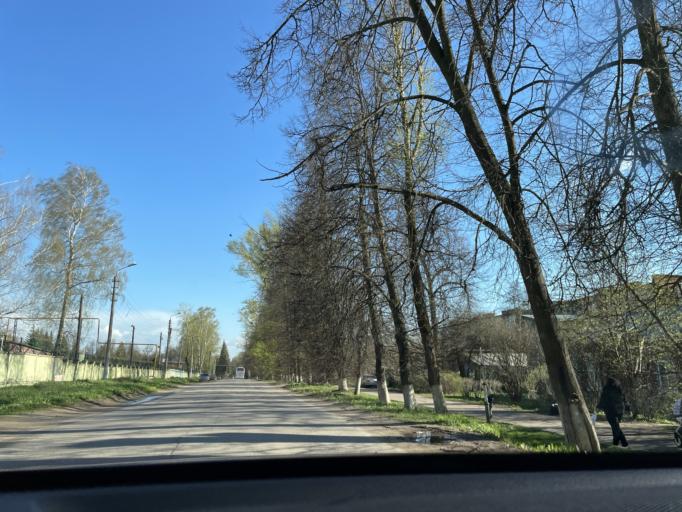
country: RU
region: Tula
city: Aleksin
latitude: 54.4883
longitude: 36.9863
